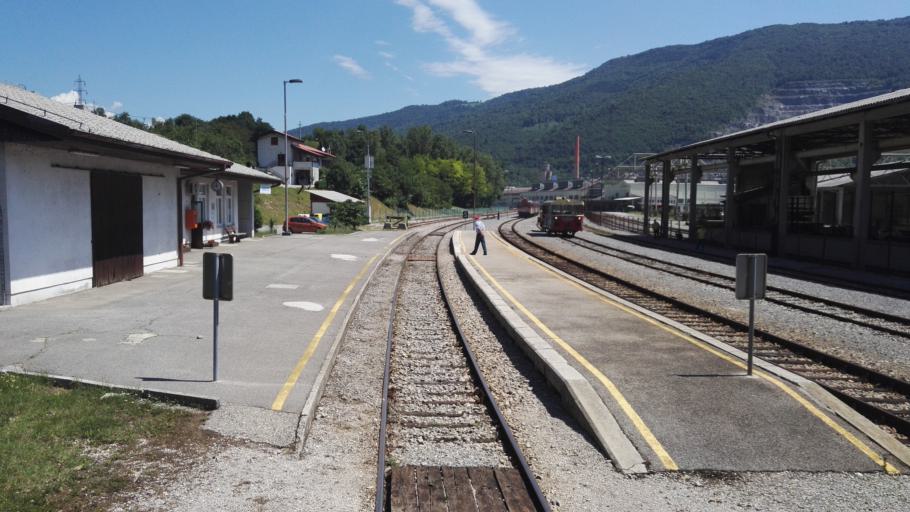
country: SI
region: Kanal
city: Deskle
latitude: 46.0580
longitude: 13.6170
